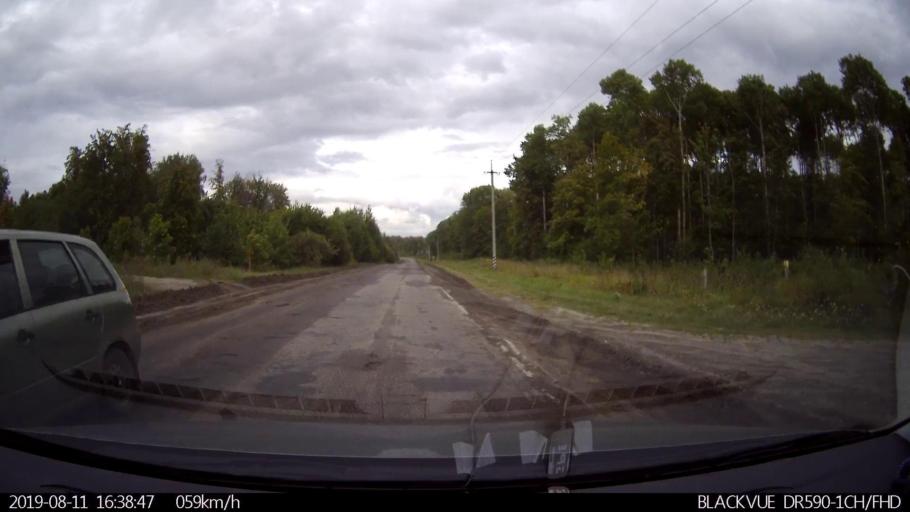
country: RU
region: Ulyanovsk
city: Mayna
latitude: 54.1368
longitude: 47.6298
